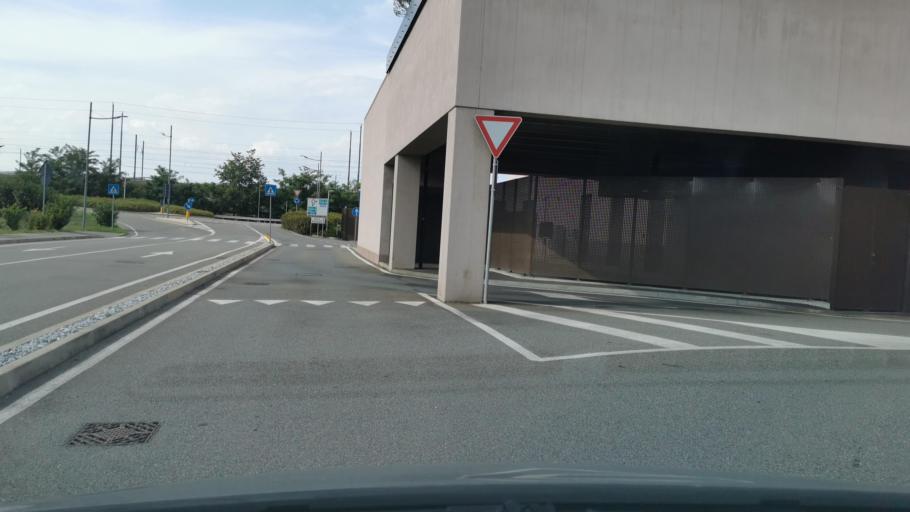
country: IT
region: Piedmont
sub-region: Provincia di Torino
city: Settimo Torinese
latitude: 45.1277
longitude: 7.7358
